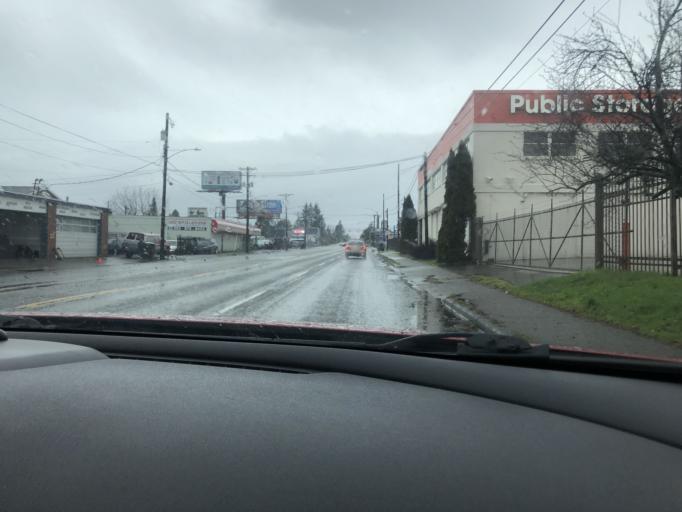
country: US
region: Washington
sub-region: Pierce County
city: Tacoma
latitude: 47.2484
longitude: -122.4629
